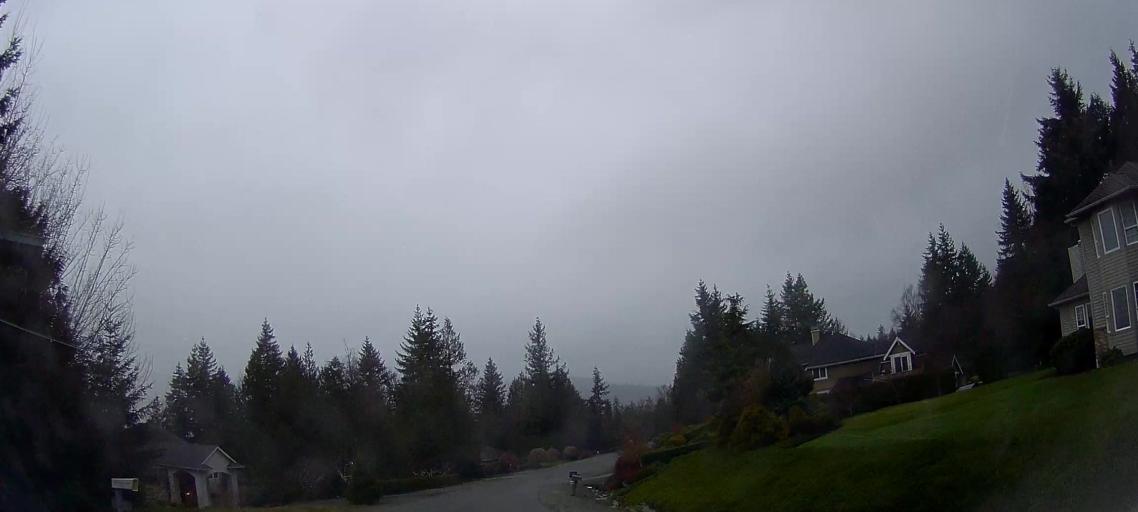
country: US
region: Washington
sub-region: Skagit County
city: Big Lake
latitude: 48.3728
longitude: -122.2943
